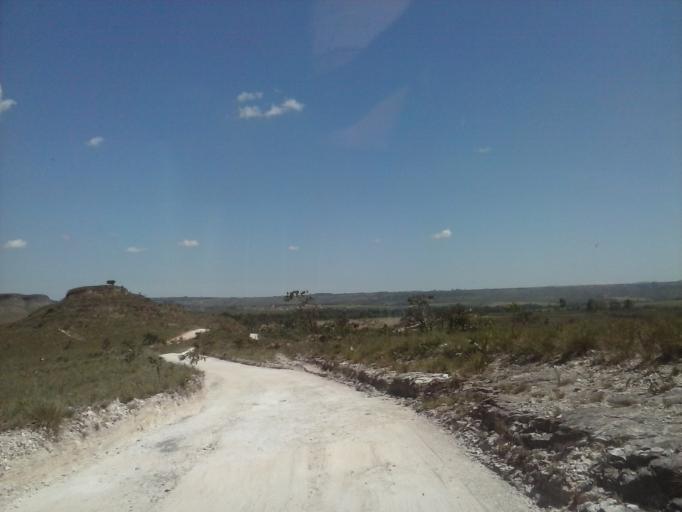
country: BR
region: Federal District
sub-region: Brasilia
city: Brasilia
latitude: -15.8861
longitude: -48.1870
